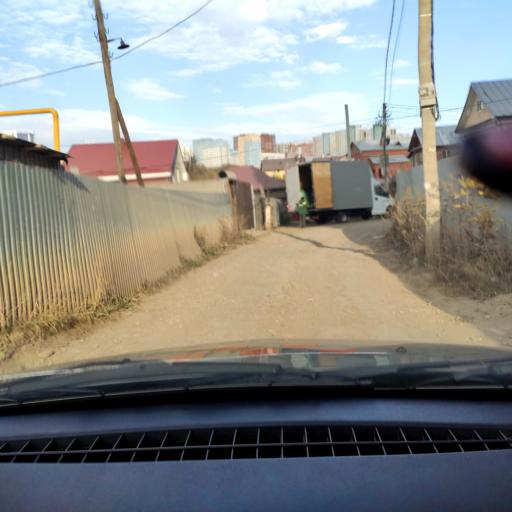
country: RU
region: Bashkortostan
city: Ufa
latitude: 54.6875
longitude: 55.9827
